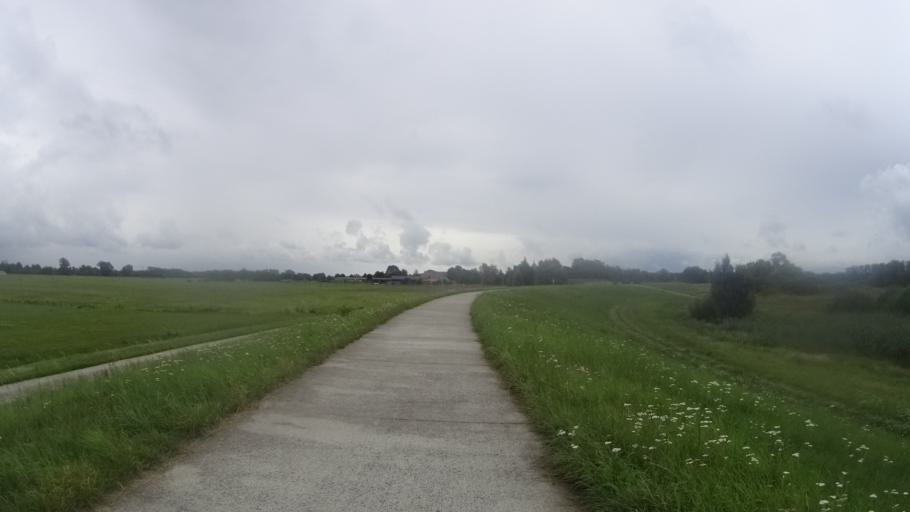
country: DE
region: Lower Saxony
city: Bleckede
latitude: 53.2946
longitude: 10.7939
